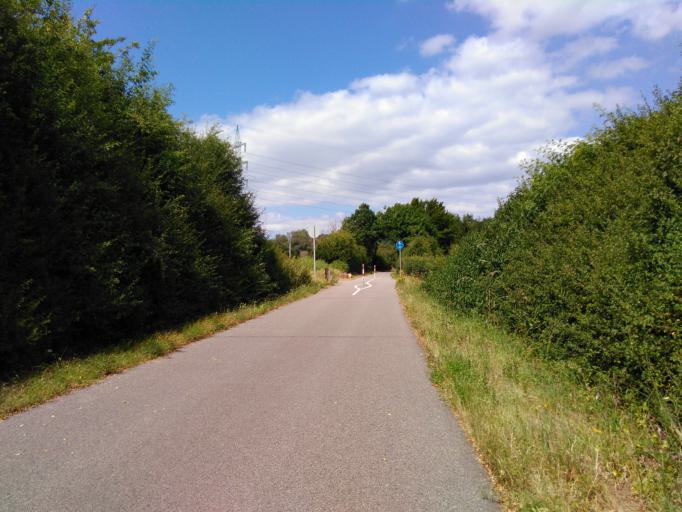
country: LU
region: Luxembourg
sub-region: Canton d'Esch-sur-Alzette
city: Petange
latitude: 49.5700
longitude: 5.8807
